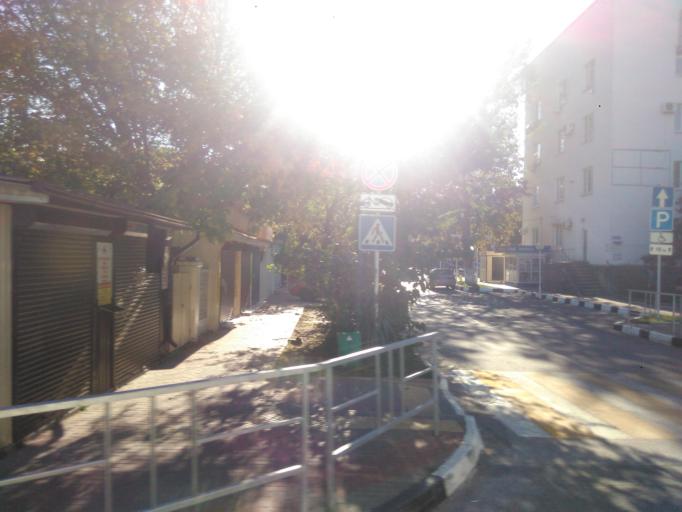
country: RU
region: Krasnodarskiy
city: Gelendzhik
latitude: 44.5564
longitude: 38.0776
